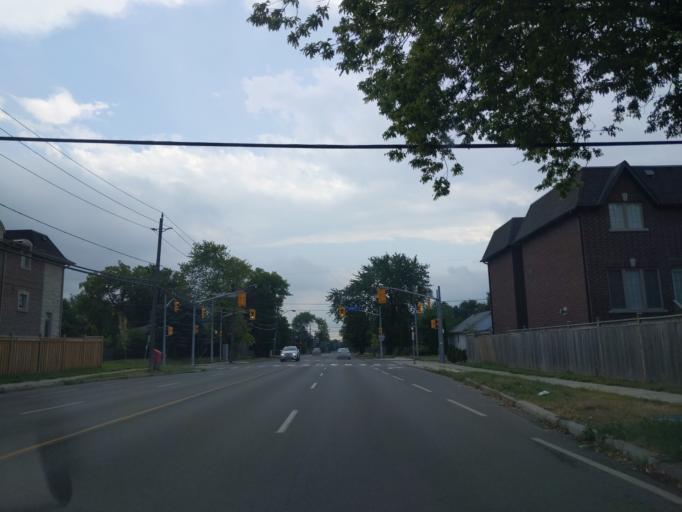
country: CA
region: Ontario
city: North York
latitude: 43.7981
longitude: -79.4140
